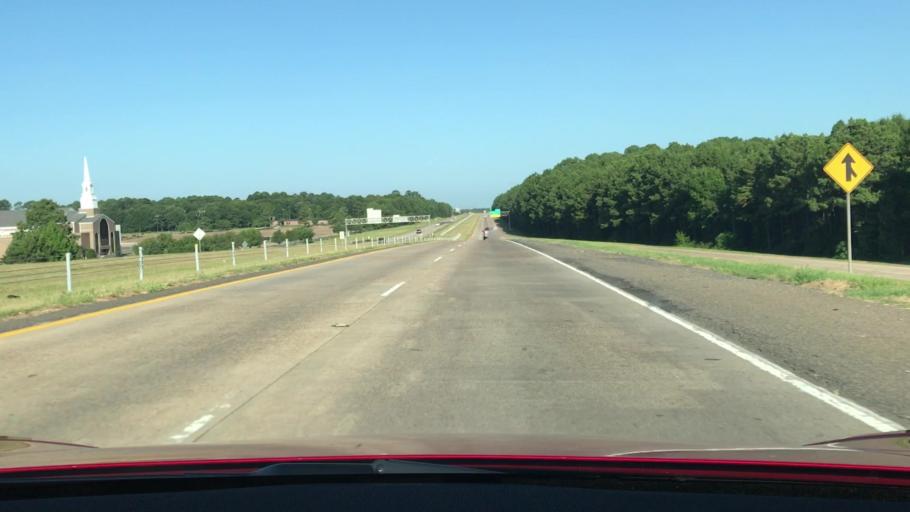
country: US
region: Louisiana
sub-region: Caddo Parish
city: Shreveport
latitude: 32.4174
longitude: -93.7982
